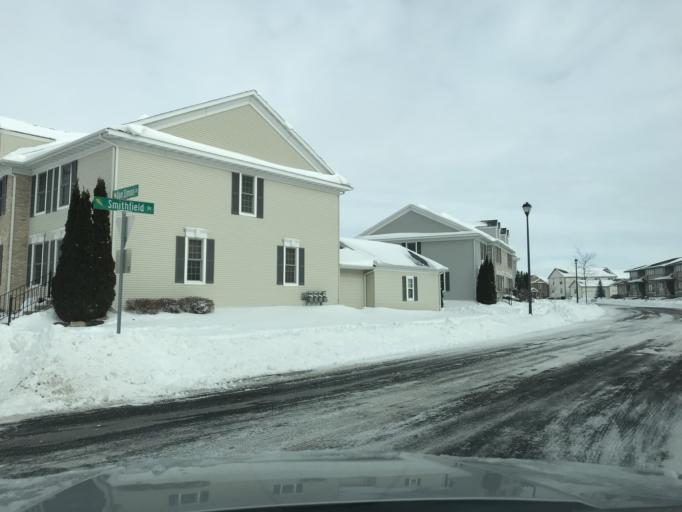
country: US
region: Wisconsin
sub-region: Dane County
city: Sun Prairie
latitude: 43.1604
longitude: -89.2620
